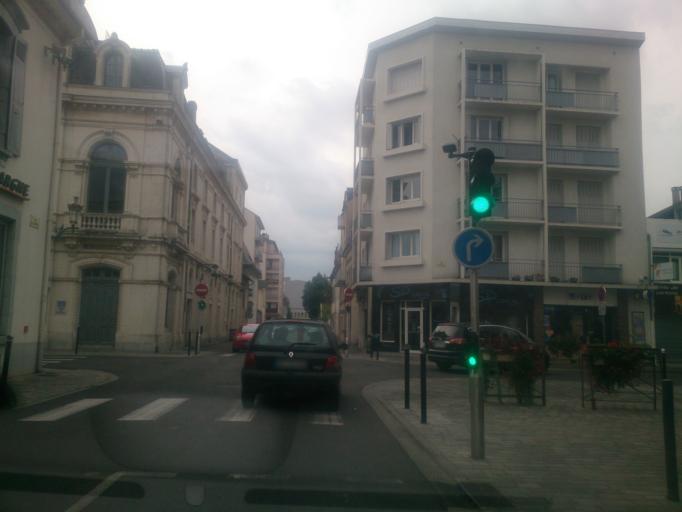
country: FR
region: Midi-Pyrenees
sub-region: Departement des Hautes-Pyrenees
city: Tarbes
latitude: 43.2306
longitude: 0.0756
